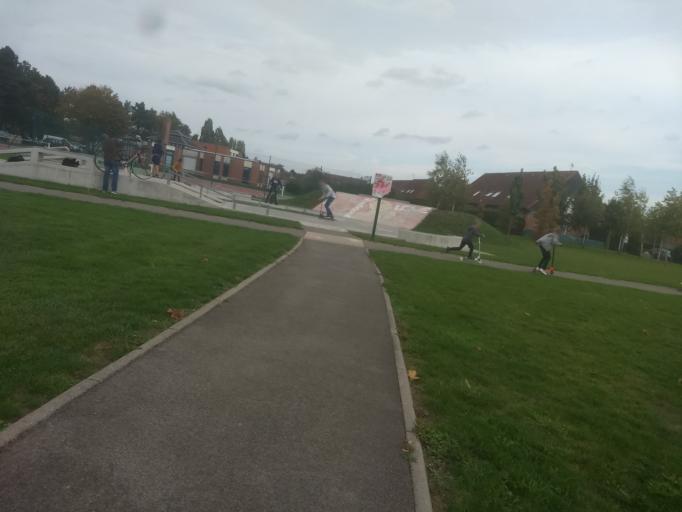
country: FR
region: Nord-Pas-de-Calais
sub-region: Departement du Pas-de-Calais
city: Beaurains
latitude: 50.2617
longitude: 2.7787
